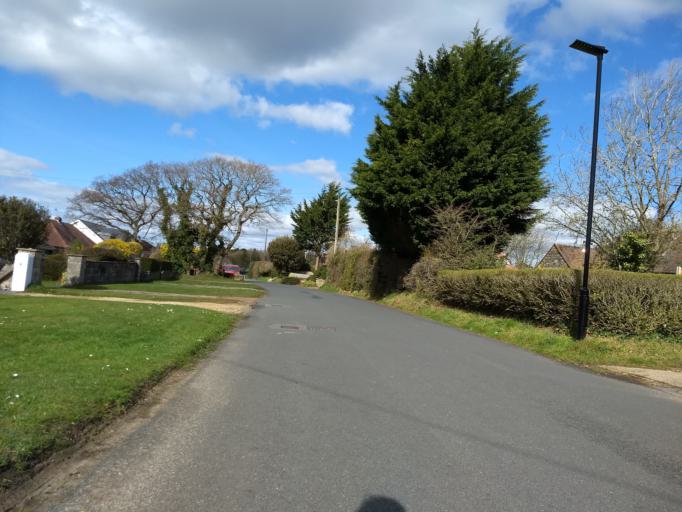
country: GB
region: England
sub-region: Isle of Wight
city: East Cowes
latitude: 50.7370
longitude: -1.2659
